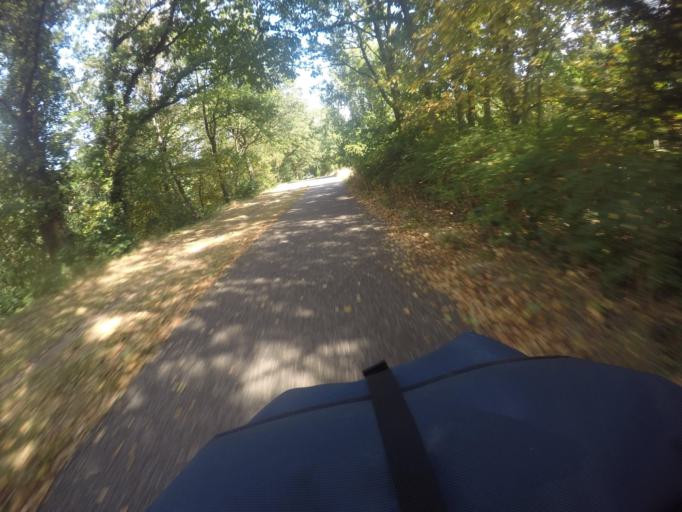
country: NL
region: Gelderland
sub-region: Gemeente Renkum
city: Oosterbeek
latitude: 51.9885
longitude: 5.8563
